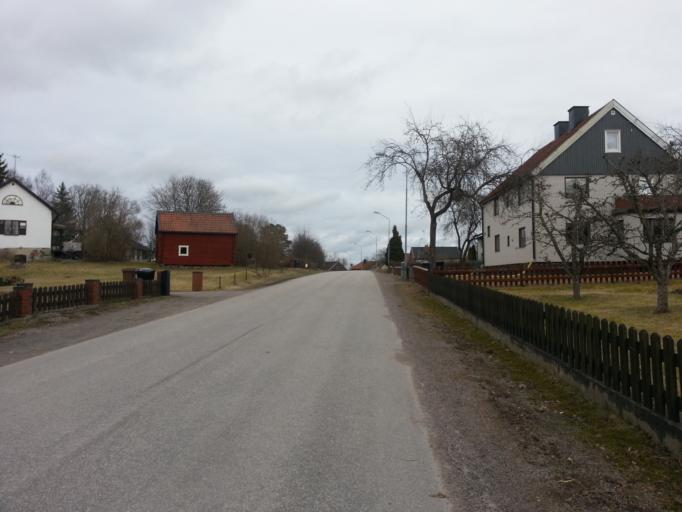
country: SE
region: Uppsala
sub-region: Osthammars Kommun
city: Gimo
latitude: 60.1696
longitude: 18.1869
